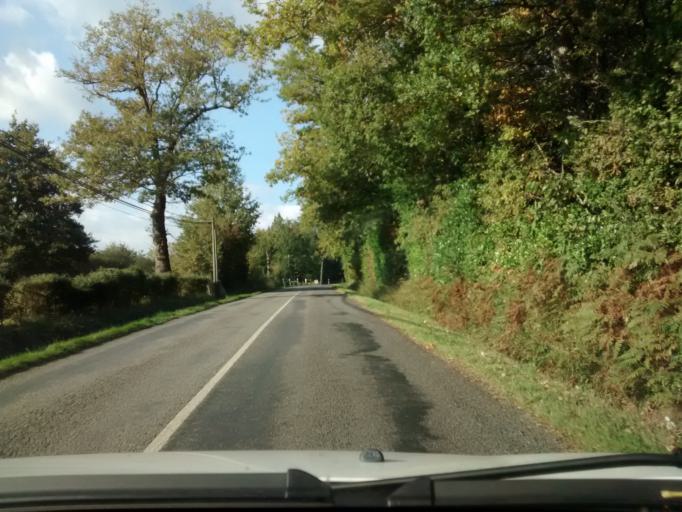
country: FR
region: Pays de la Loire
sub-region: Departement de la Loire-Atlantique
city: Sautron
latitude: 47.2721
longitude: -1.6717
